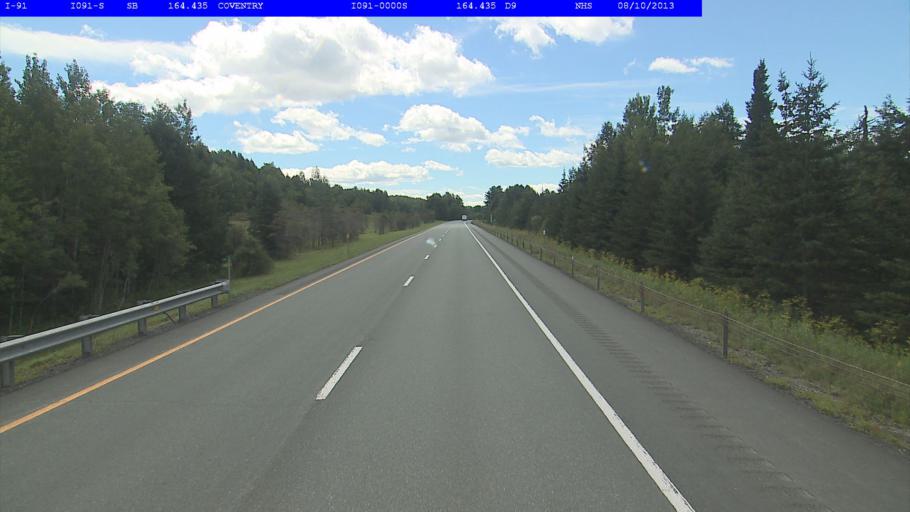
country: US
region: Vermont
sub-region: Orleans County
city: Newport
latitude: 44.8469
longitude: -72.1937
